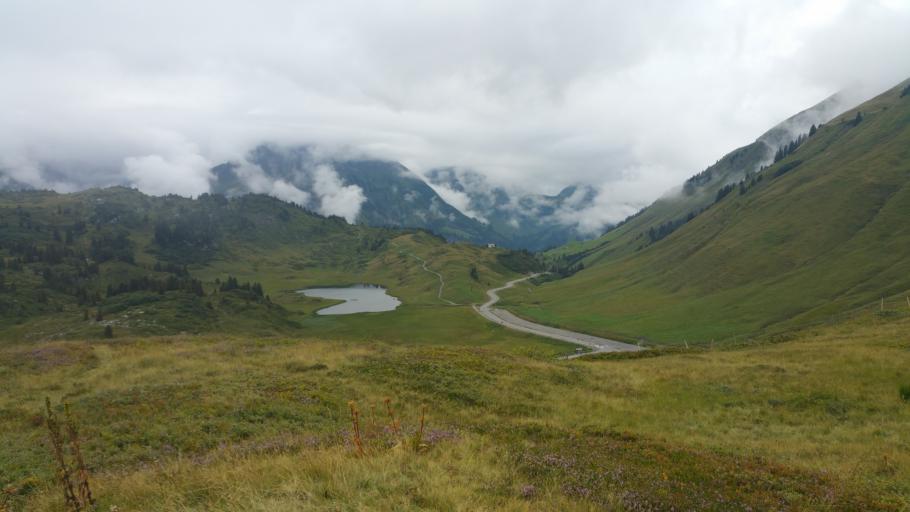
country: AT
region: Vorarlberg
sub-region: Politischer Bezirk Bregenz
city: Schroecken
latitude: 47.2685
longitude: 10.1331
